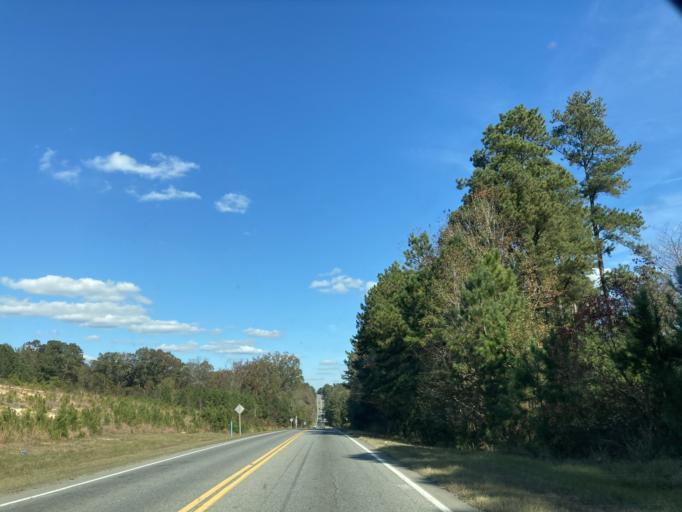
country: US
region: Georgia
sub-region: Bibb County
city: Macon
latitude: 32.8929
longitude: -83.5330
